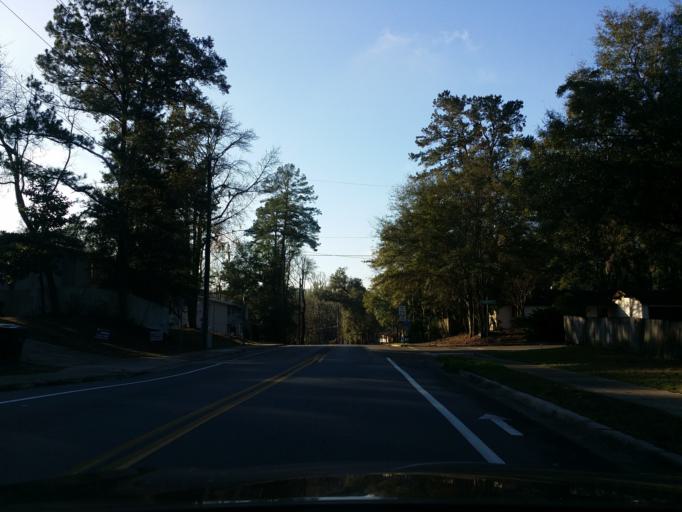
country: US
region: Florida
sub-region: Leon County
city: Tallahassee
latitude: 30.4345
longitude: -84.2125
